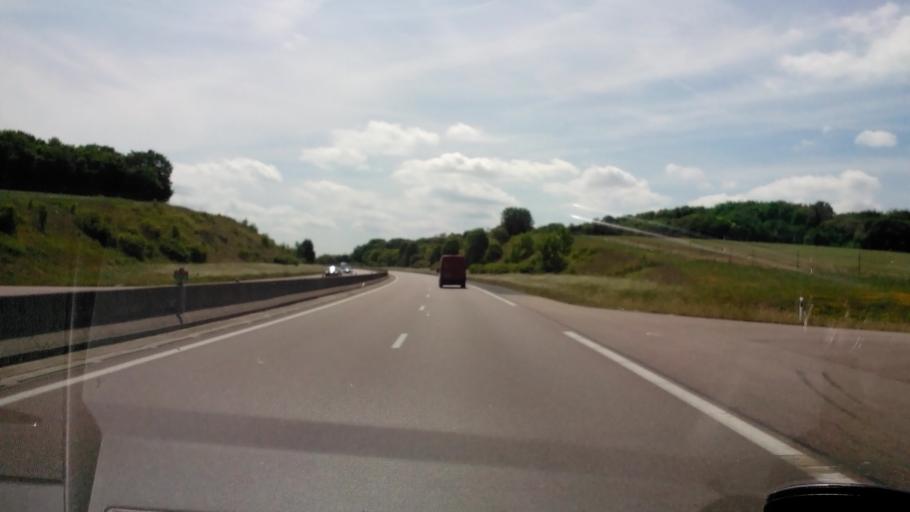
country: FR
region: Lorraine
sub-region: Departement des Vosges
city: Chatenois
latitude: 48.4112
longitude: 5.8669
